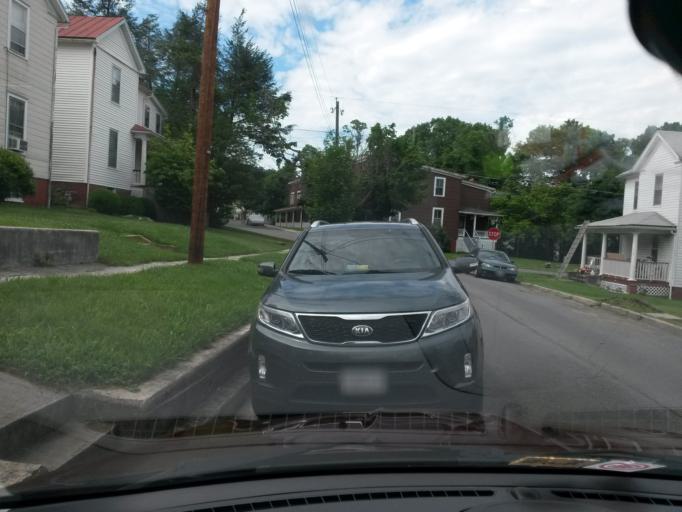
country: US
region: Virginia
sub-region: Alleghany County
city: Clifton Forge
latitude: 37.8204
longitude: -79.8290
